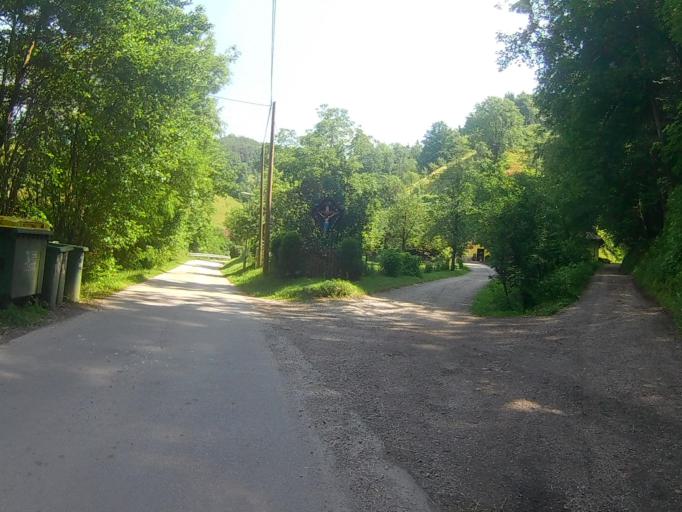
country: SI
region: Maribor
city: Bresternica
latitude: 46.5748
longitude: 15.5790
